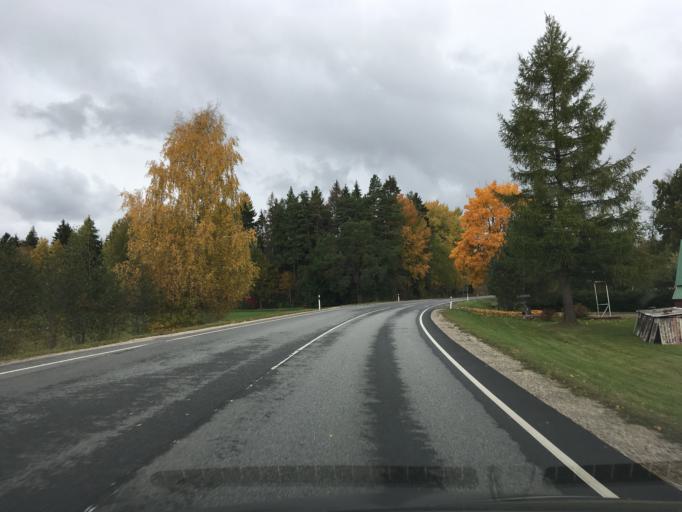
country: EE
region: Harju
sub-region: Anija vald
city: Kehra
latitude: 59.3125
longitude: 25.3439
